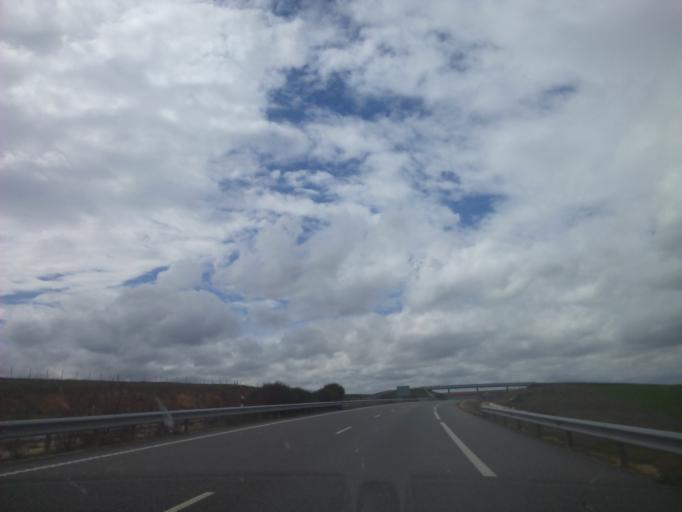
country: ES
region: Castille and Leon
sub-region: Provincia de Salamanca
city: Machacon
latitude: 40.9191
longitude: -5.5217
